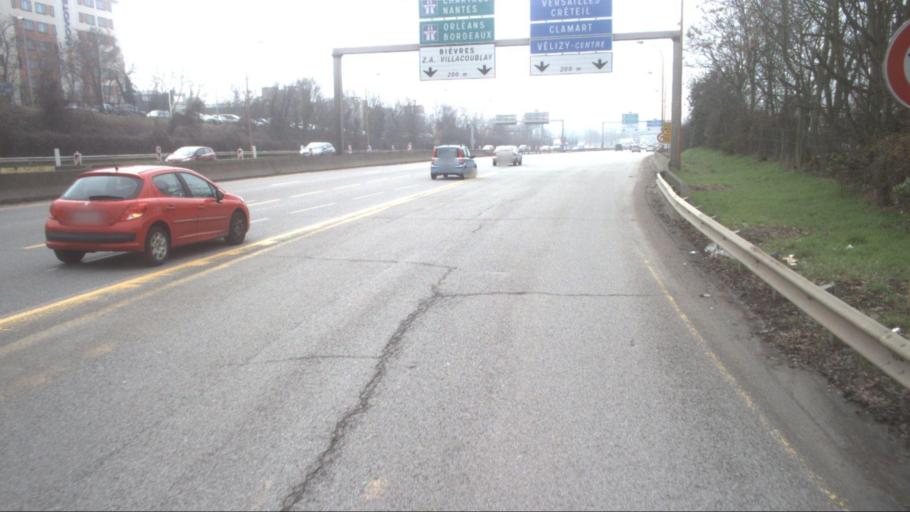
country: FR
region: Ile-de-France
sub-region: Departement de l'Essonne
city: Bievres
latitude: 48.7836
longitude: 2.2229
